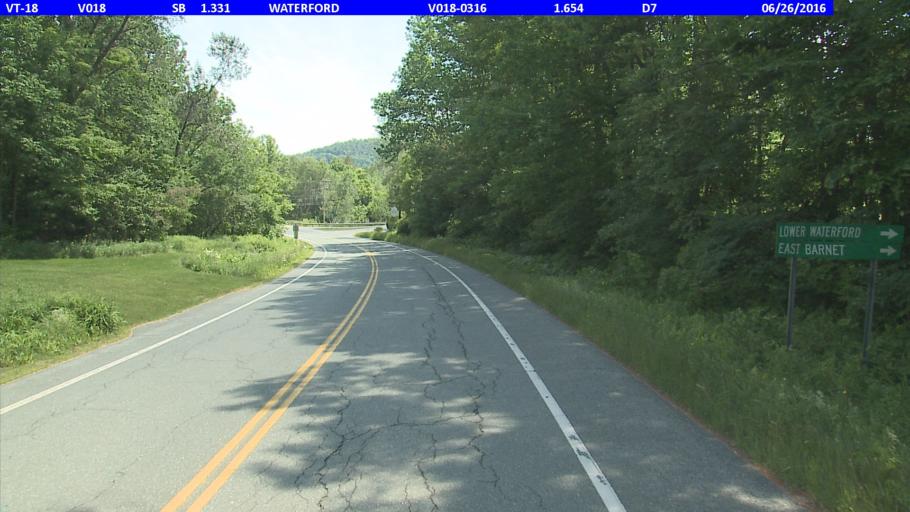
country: US
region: Vermont
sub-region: Caledonia County
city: Saint Johnsbury
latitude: 44.3562
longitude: -71.9070
